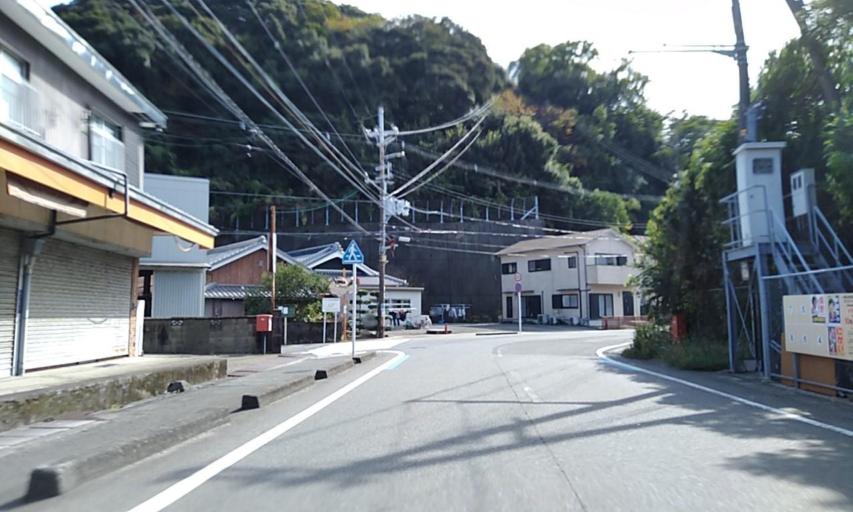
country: JP
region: Wakayama
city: Gobo
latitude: 33.9627
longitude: 135.1137
